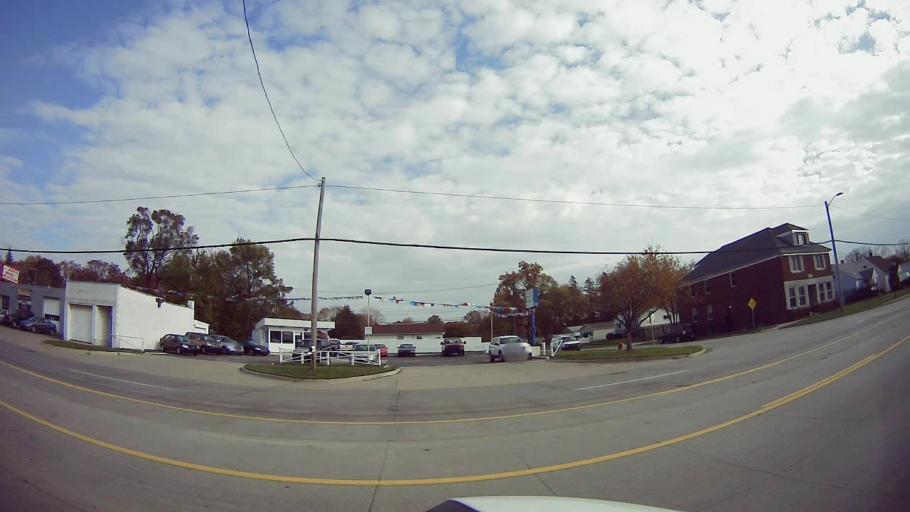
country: US
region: Michigan
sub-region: Macomb County
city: Warren
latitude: 42.4702
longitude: -83.0646
